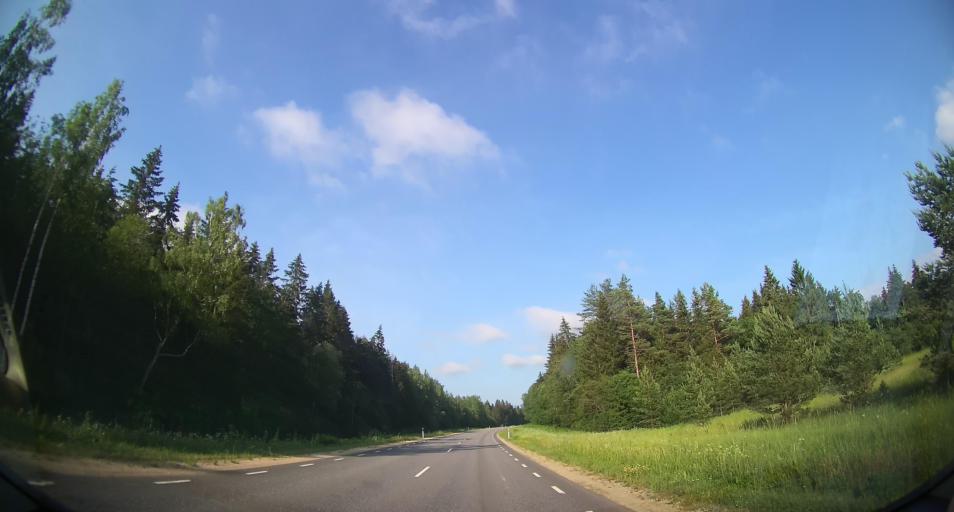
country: EE
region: Harju
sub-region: Anija vald
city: Kehra
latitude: 59.2199
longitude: 25.2393
